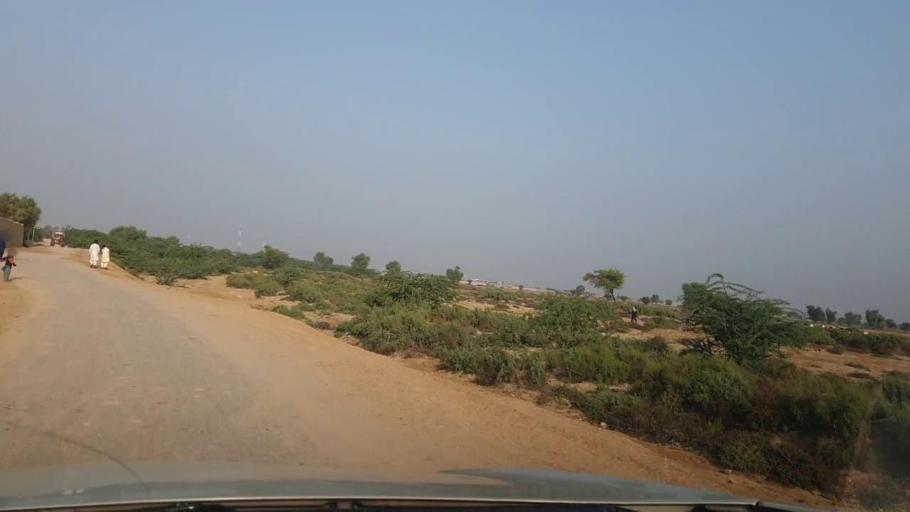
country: PK
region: Sindh
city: Sehwan
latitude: 26.3360
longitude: 67.7304
